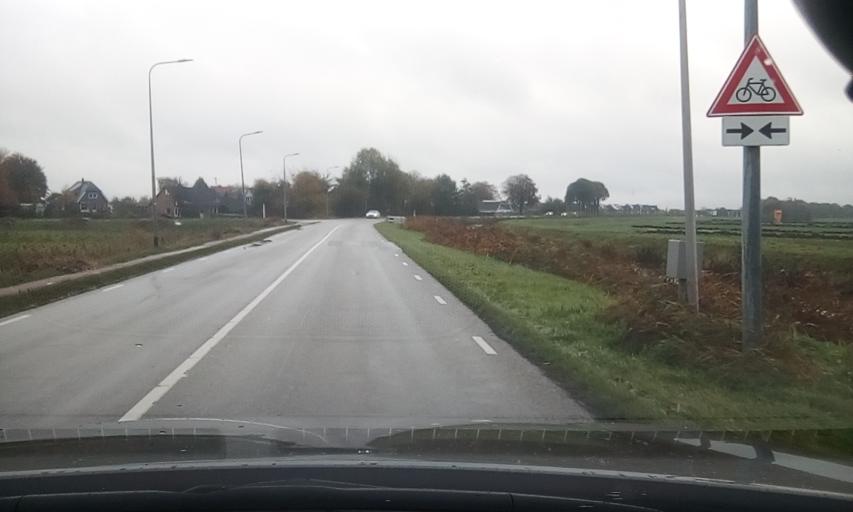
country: NL
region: Groningen
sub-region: Gemeente Groningen
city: Oosterpark
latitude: 53.2304
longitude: 6.6375
